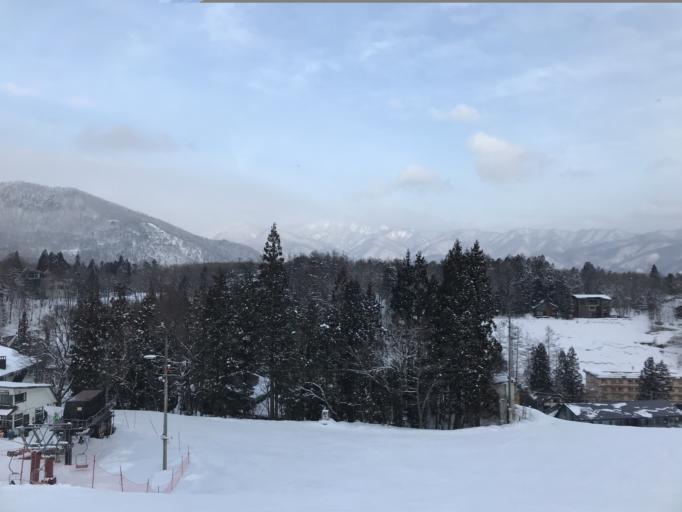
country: JP
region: Nagano
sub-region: Kitaazumi Gun
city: Hakuba
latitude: 36.7033
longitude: 137.8345
